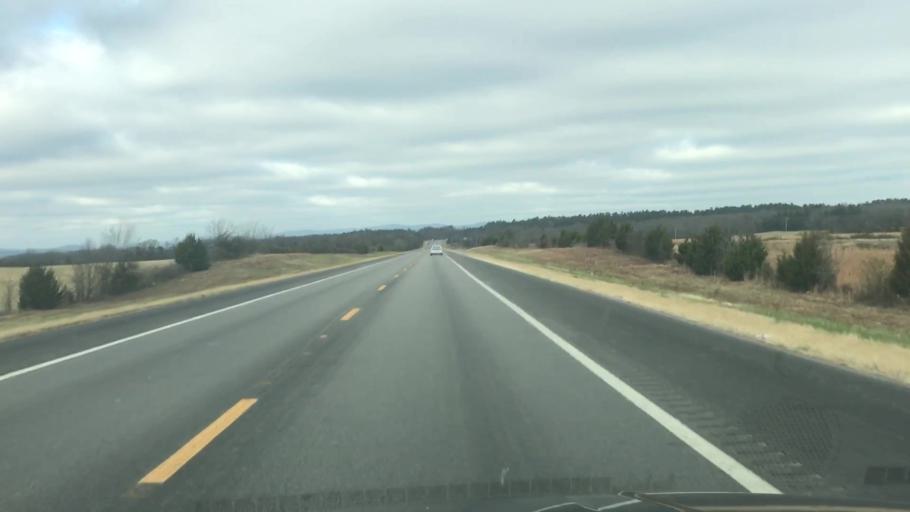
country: US
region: Arkansas
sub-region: Scott County
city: Waldron
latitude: 34.8749
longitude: -94.0909
